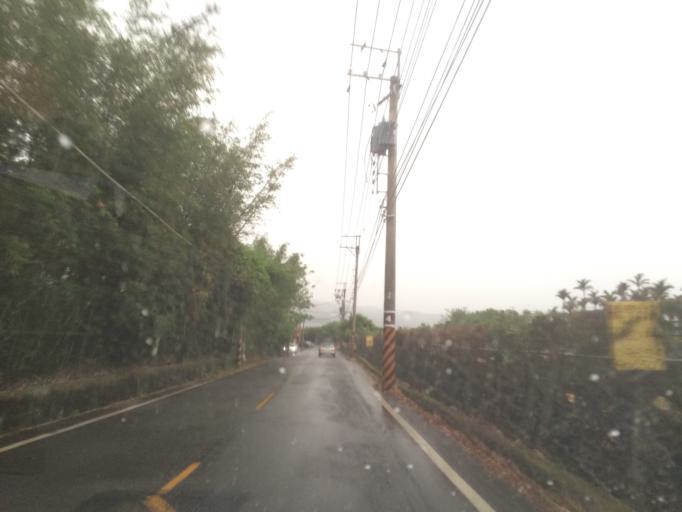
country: TW
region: Taiwan
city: Fengyuan
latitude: 24.1997
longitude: 120.8001
